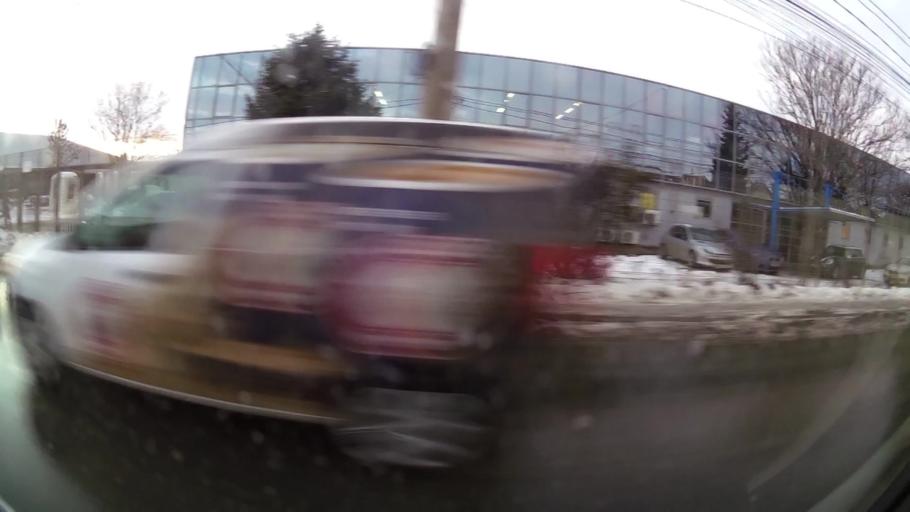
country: RO
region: Ilfov
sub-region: Comuna Popesti-Leordeni
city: Popesti-Leordeni
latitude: 44.3761
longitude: 26.1567
